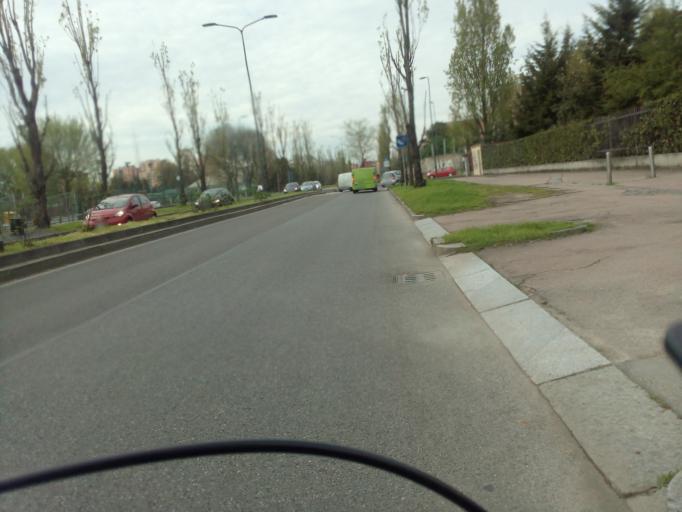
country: IT
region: Lombardy
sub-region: Citta metropolitana di Milano
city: Cesano Boscone
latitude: 45.4653
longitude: 9.1133
